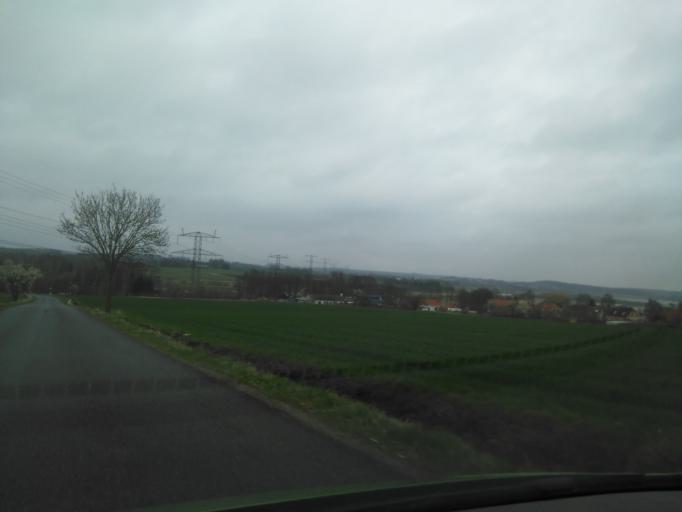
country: DK
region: Central Jutland
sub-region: Arhus Kommune
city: Kolt
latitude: 56.1284
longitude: 10.0419
